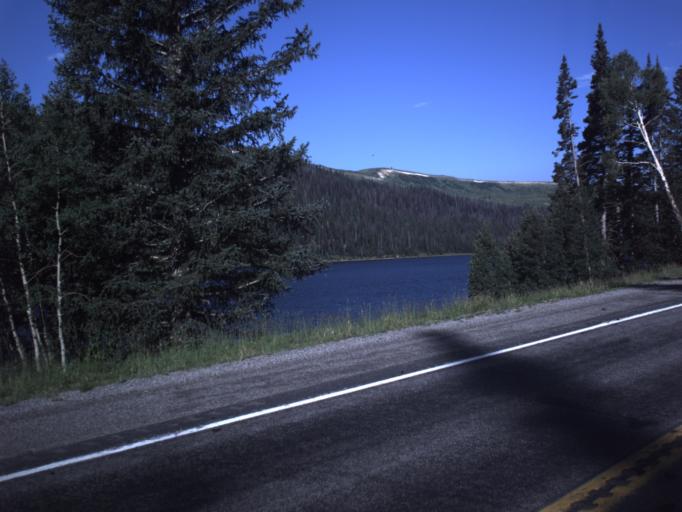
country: US
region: Utah
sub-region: Sanpete County
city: Fairview
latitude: 39.5928
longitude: -111.2661
